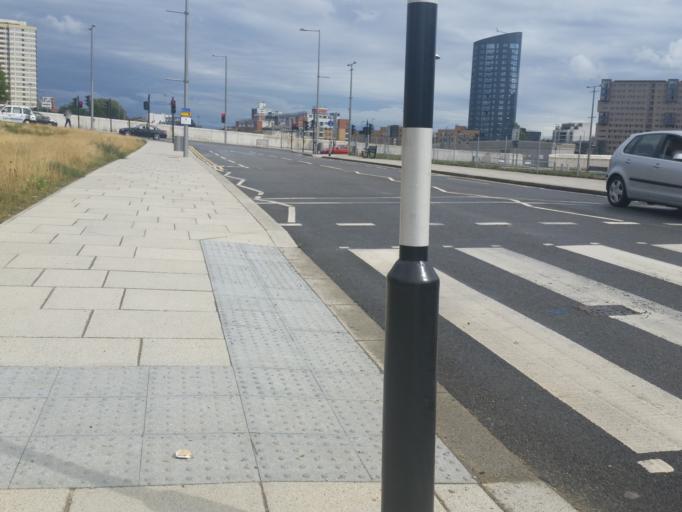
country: GB
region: England
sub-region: Greater London
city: Poplar
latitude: 51.5455
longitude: -0.0050
